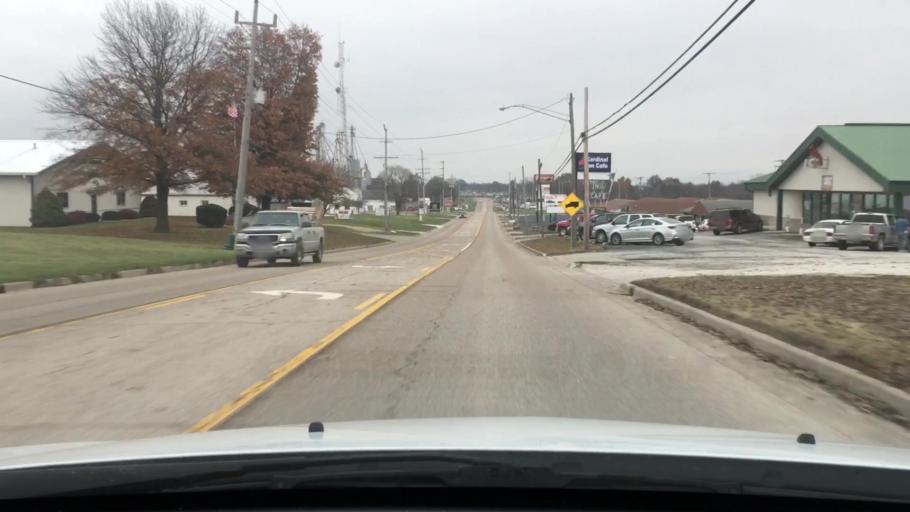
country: US
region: Illinois
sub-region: Pike County
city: Pittsfield
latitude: 39.6046
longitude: -90.8358
